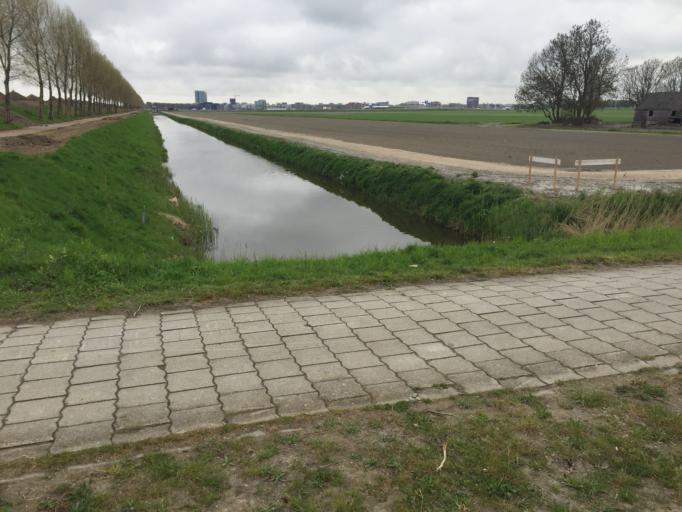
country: NL
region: North Holland
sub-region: Gemeente Aalsmeer
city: Aalsmeer
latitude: 52.2742
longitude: 4.7268
